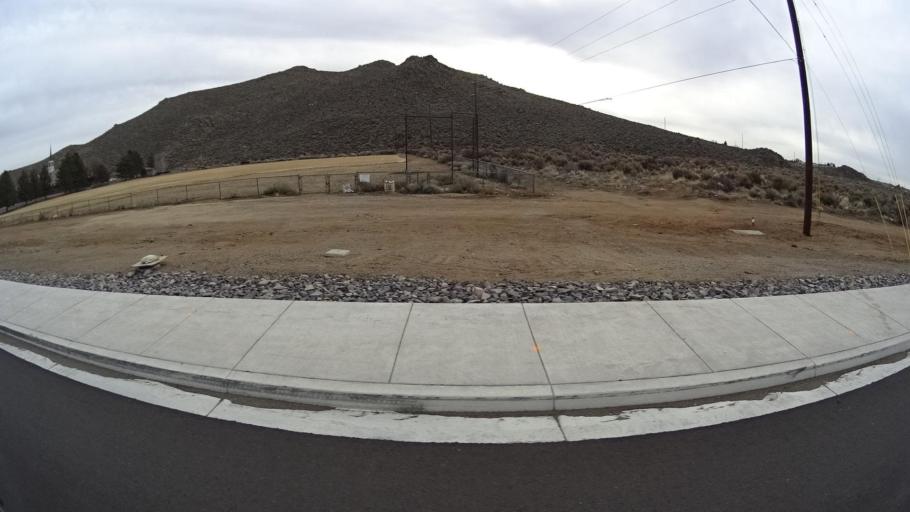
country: US
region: Nevada
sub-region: Washoe County
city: Lemmon Valley
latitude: 39.6218
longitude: -119.8485
